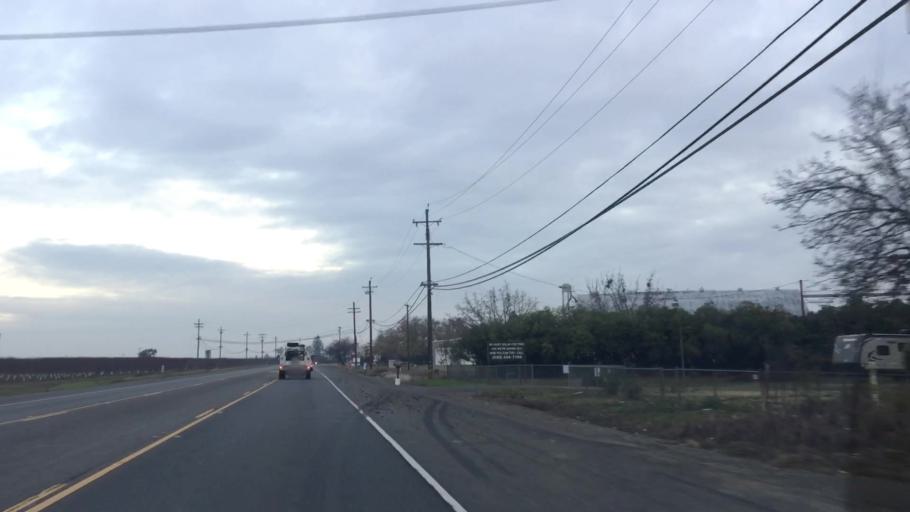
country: US
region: California
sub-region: Yuba County
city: Marysville
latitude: 39.2156
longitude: -121.5998
